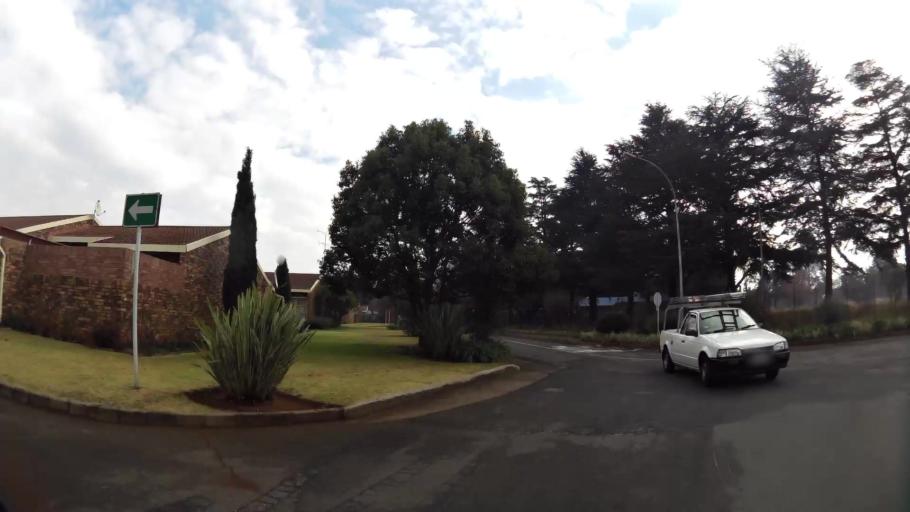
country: ZA
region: Gauteng
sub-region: Sedibeng District Municipality
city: Vanderbijlpark
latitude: -26.7048
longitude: 27.8312
